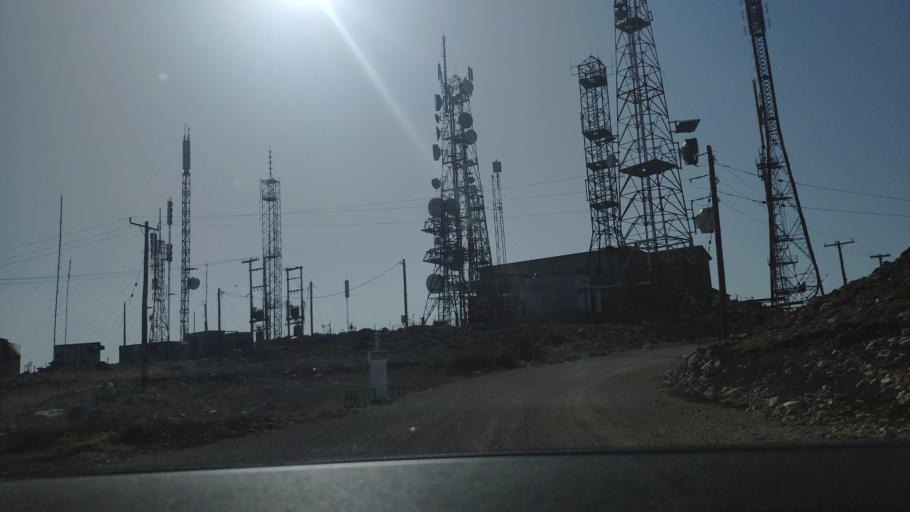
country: GR
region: West Greece
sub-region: Nomos Aitolias kai Akarnanias
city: Monastirakion
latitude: 38.8082
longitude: 20.9842
